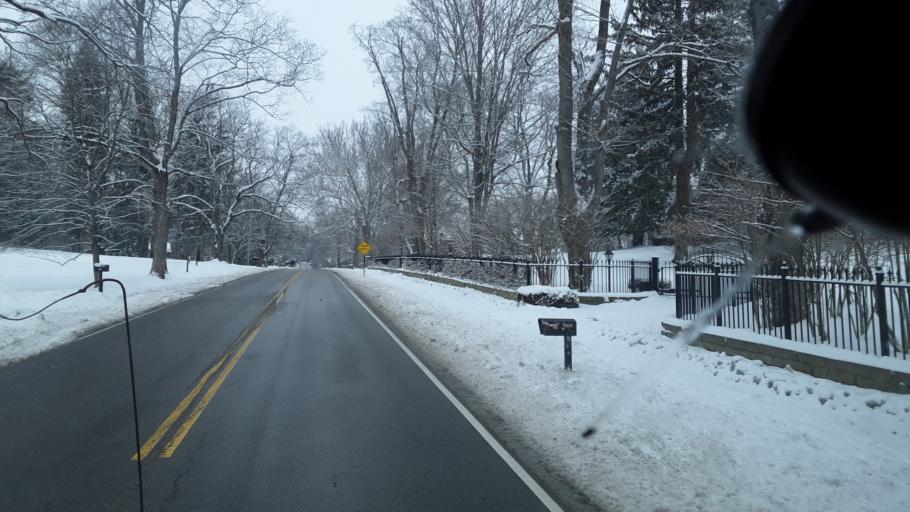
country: US
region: Ohio
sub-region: Licking County
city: Granville
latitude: 40.0668
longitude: -82.5050
